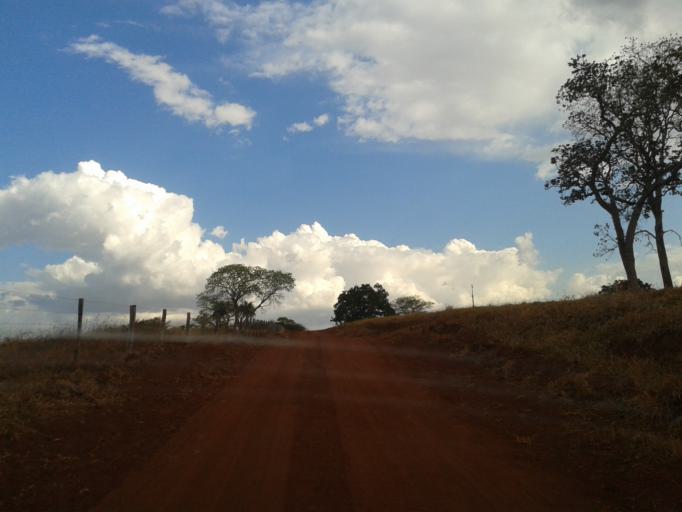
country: BR
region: Minas Gerais
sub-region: Santa Vitoria
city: Santa Vitoria
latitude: -19.1757
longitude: -49.9456
